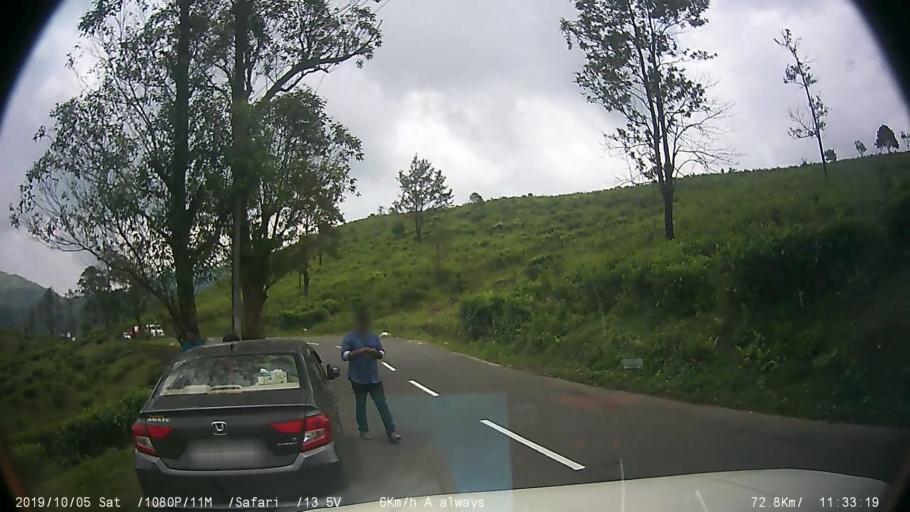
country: IN
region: Kerala
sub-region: Kottayam
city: Erattupetta
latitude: 9.5868
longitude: 76.9680
